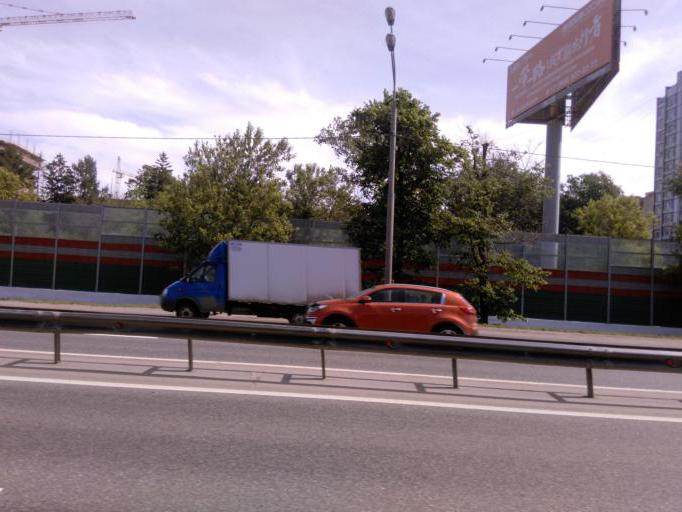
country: RU
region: Moscow
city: Khimki
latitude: 55.8924
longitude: 37.4312
